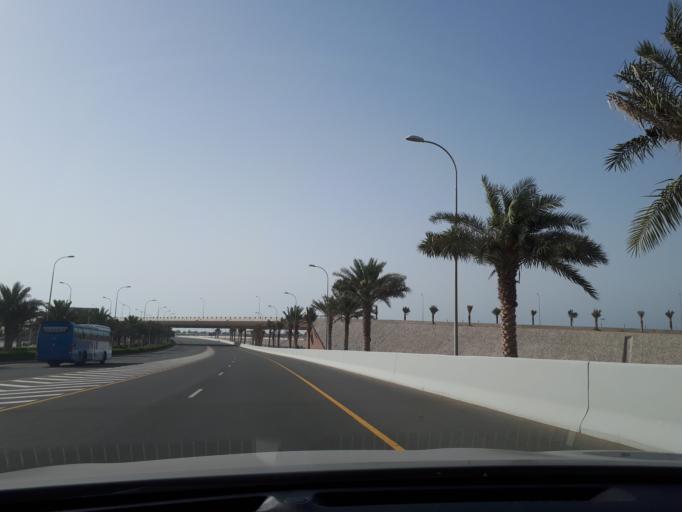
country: OM
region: Muhafazat Masqat
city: Bawshar
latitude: 23.5961
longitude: 58.3312
